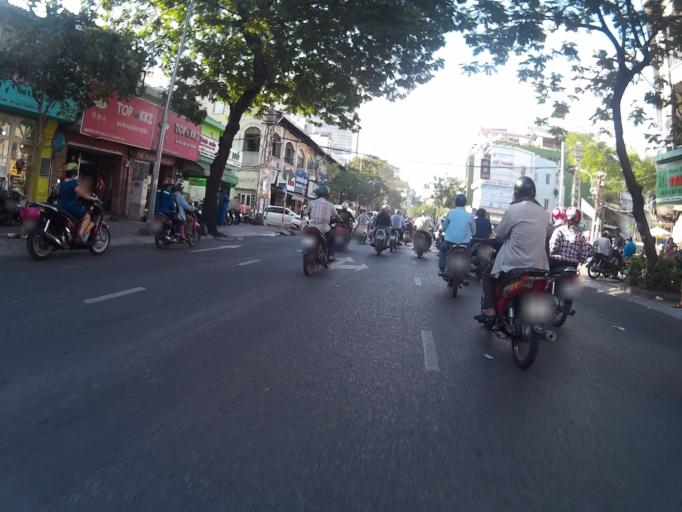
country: VN
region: Ho Chi Minh City
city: Quan Mot
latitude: 10.7907
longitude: 106.6973
